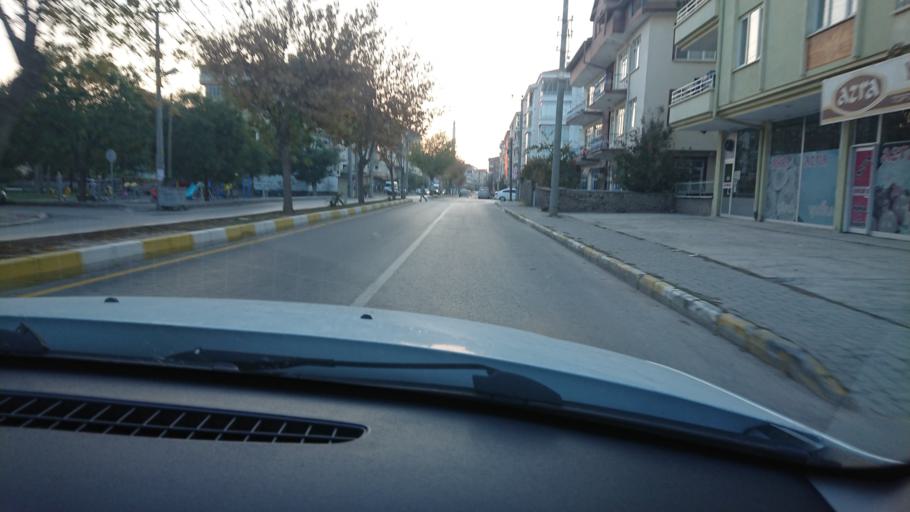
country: TR
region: Aksaray
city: Aksaray
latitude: 38.3616
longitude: 34.0268
